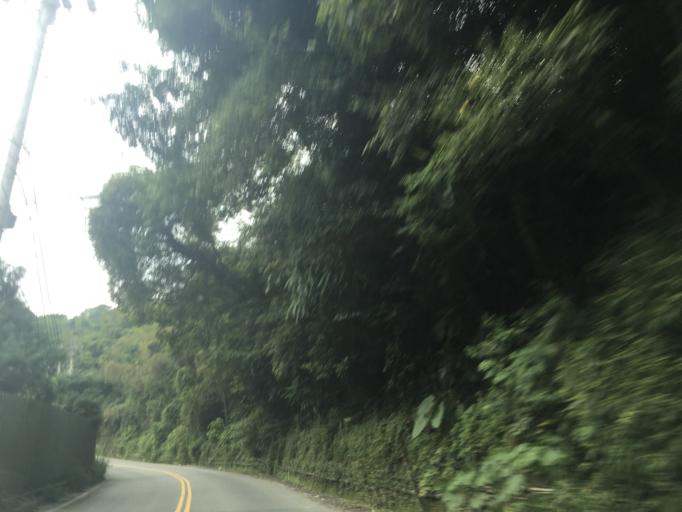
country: TW
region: Taiwan
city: Fengyuan
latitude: 24.3304
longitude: 120.9202
